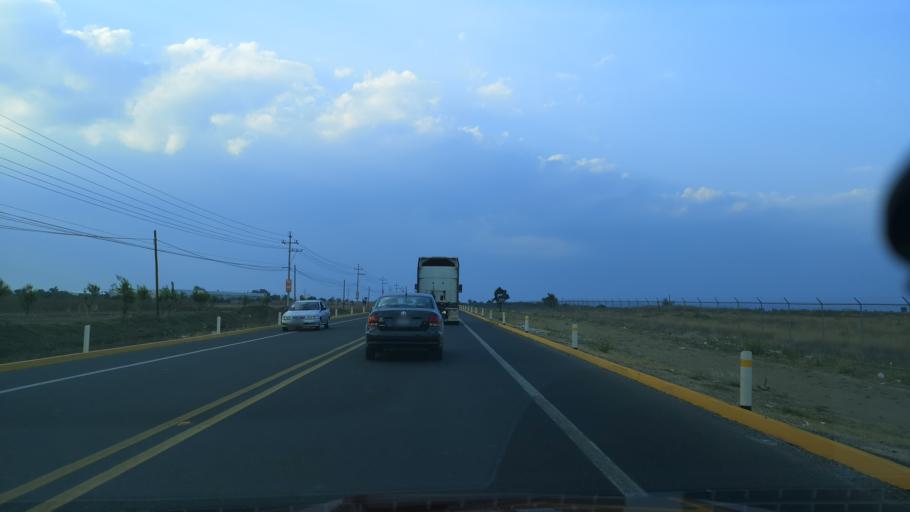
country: MX
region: Puebla
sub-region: Juan C. Bonilla
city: Santa Maria Zacatepec
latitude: 19.1472
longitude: -98.3741
